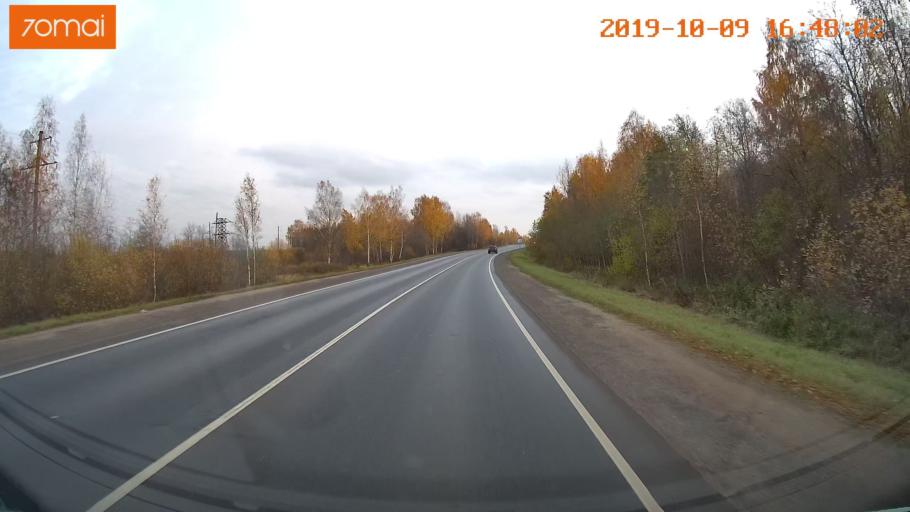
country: RU
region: Kostroma
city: Volgorechensk
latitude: 57.4322
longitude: 41.1869
